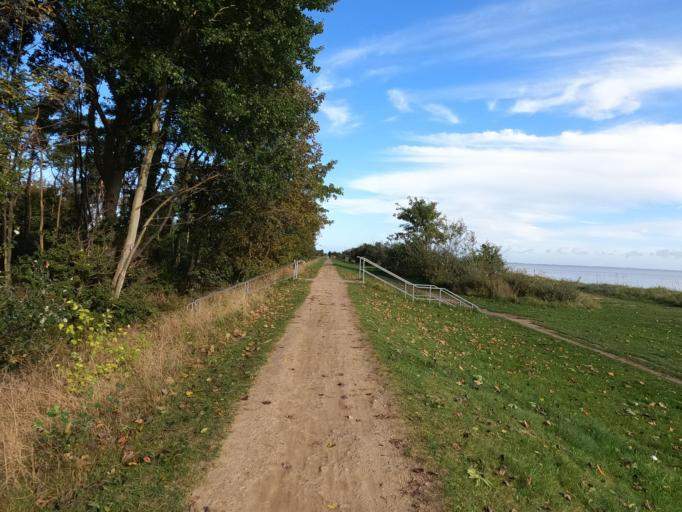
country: DE
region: Schleswig-Holstein
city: Dahme
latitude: 54.2688
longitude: 11.0827
